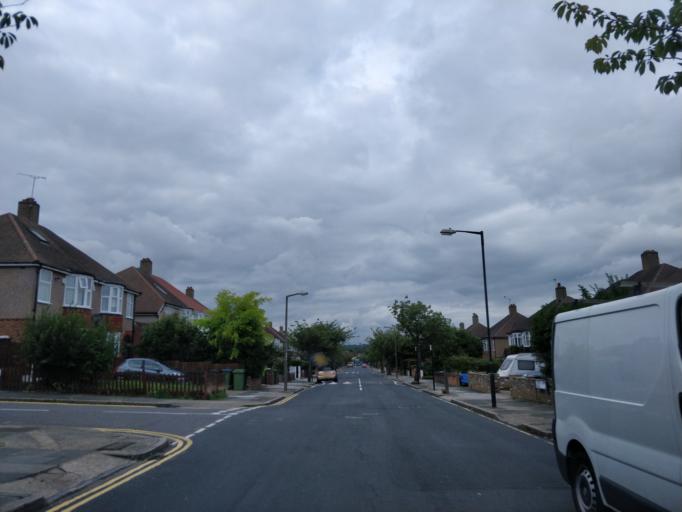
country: GB
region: England
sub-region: Greater London
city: Chislehurst
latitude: 51.4332
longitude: 0.0512
